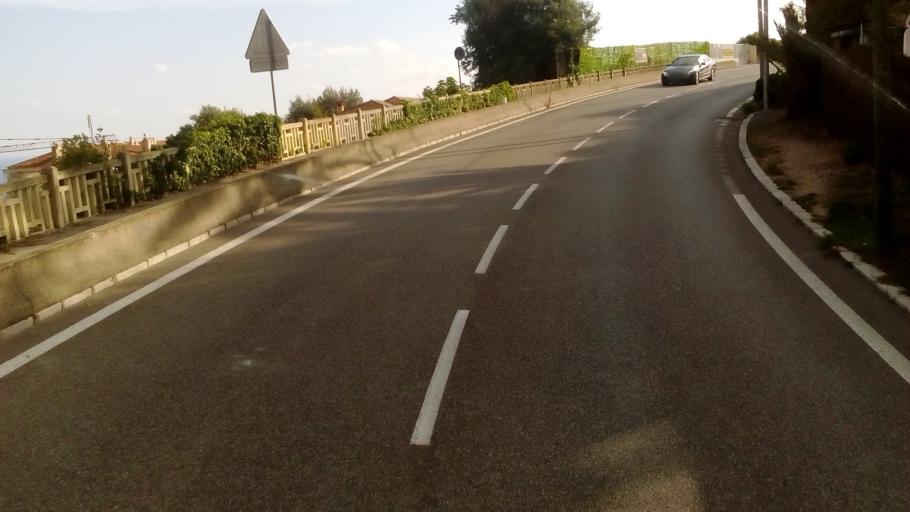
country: MC
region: Commune de Monaco
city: Saint-Roman
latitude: 43.7525
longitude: 7.4321
